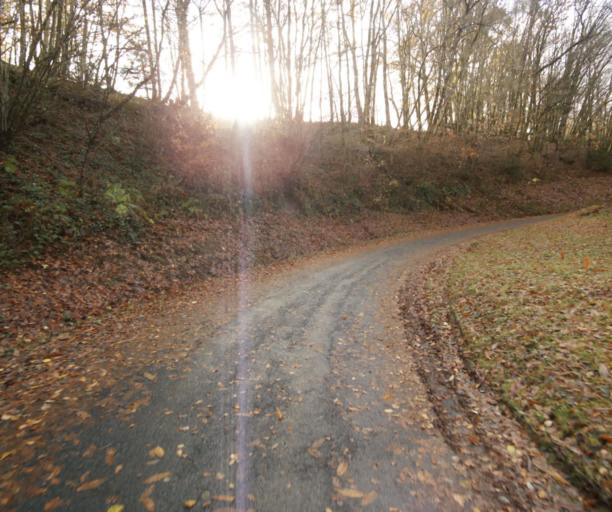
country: FR
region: Limousin
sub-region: Departement de la Correze
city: Sainte-Fereole
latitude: 45.2111
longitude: 1.6311
